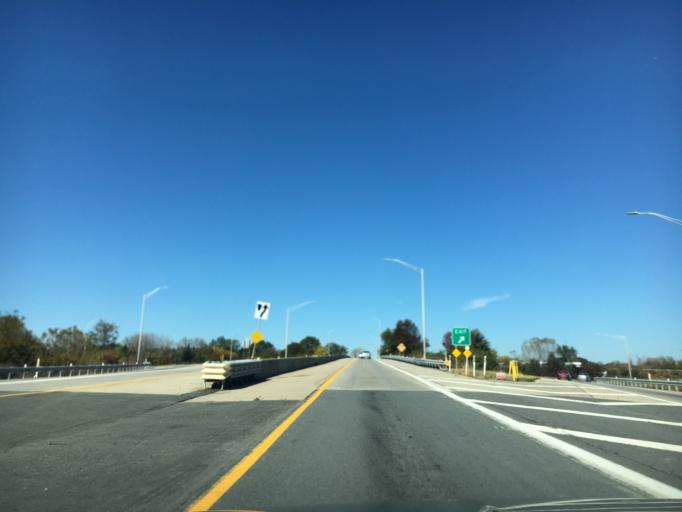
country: US
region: Pennsylvania
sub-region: Northampton County
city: Bethlehem
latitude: 40.6468
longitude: -75.4138
